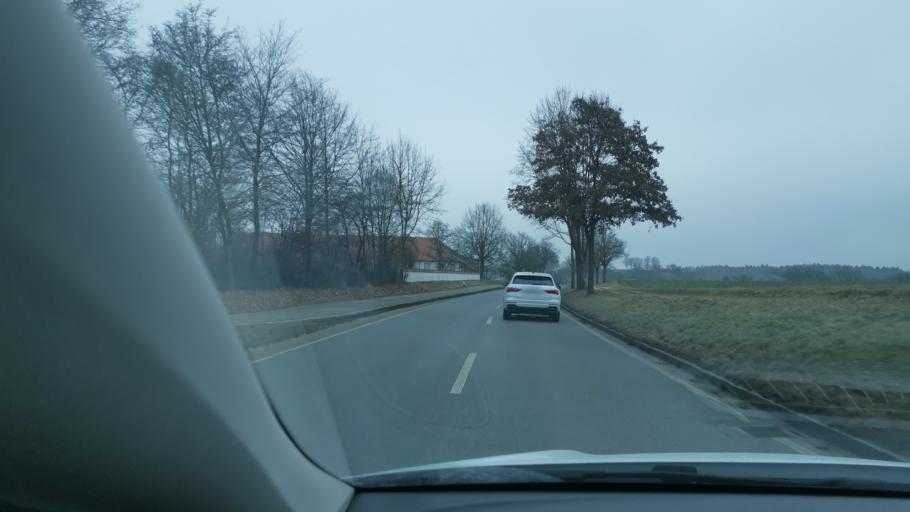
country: DE
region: Bavaria
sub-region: Swabia
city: Thierhaupten
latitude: 48.5587
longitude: 10.9108
